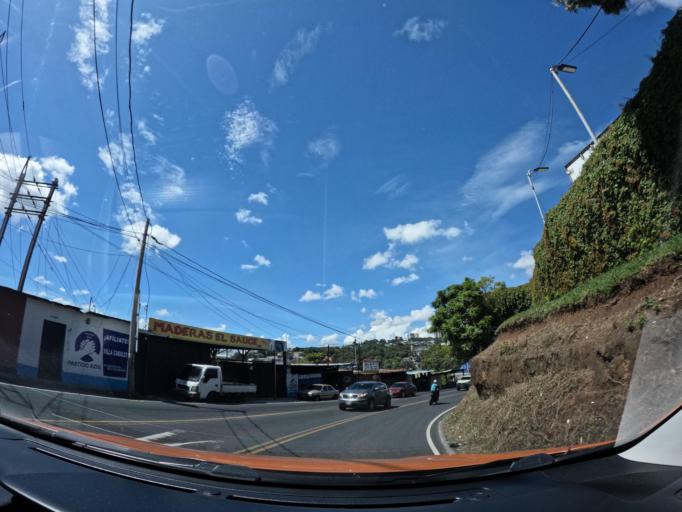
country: GT
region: Guatemala
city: Santa Catarina Pinula
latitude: 14.5538
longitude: -90.5276
